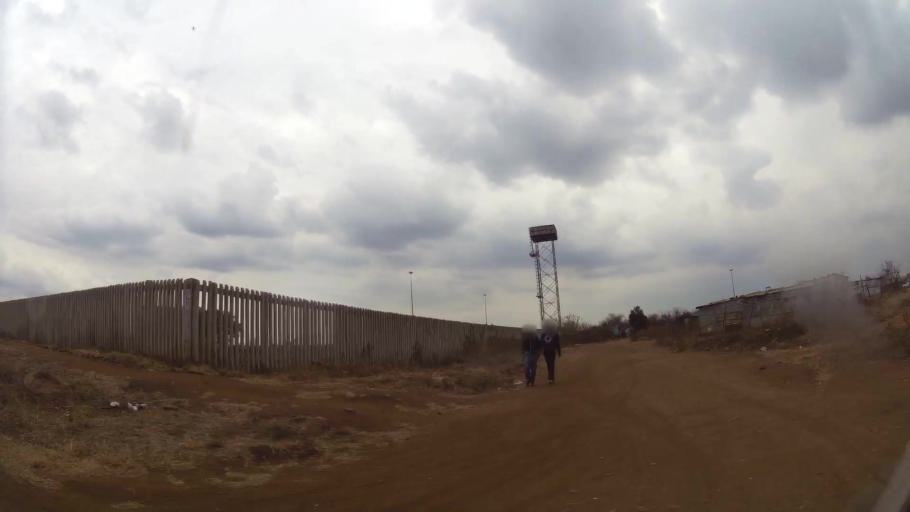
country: ZA
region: Gauteng
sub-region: Ekurhuleni Metropolitan Municipality
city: Germiston
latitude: -26.3682
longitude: 28.1493
